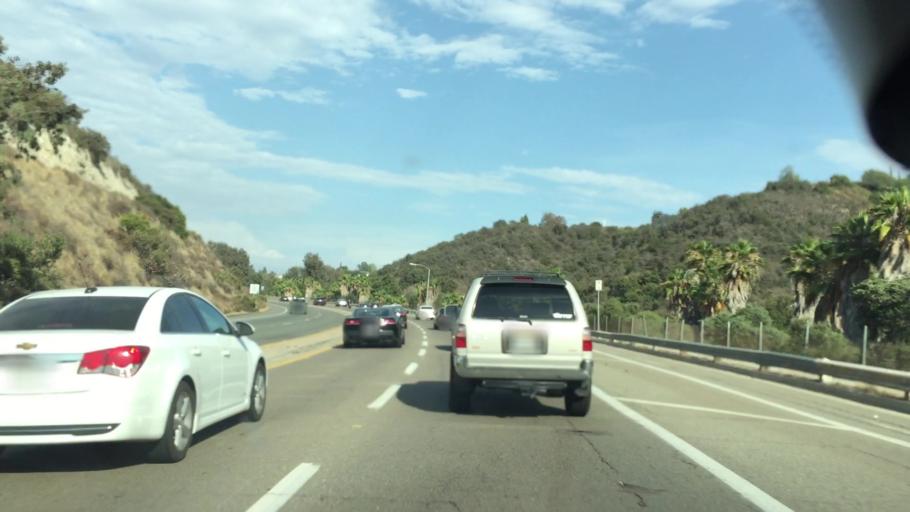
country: US
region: California
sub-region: San Diego County
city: Lemon Grove
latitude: 32.7703
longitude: -117.0920
